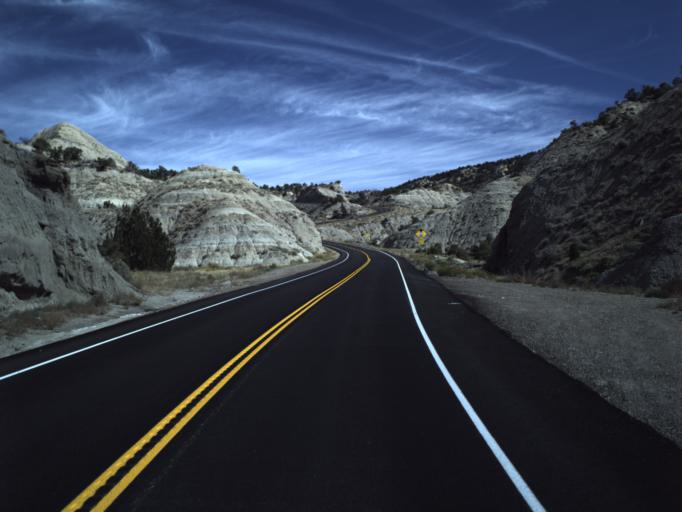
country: US
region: Utah
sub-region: Garfield County
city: Panguitch
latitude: 37.6270
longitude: -111.8503
